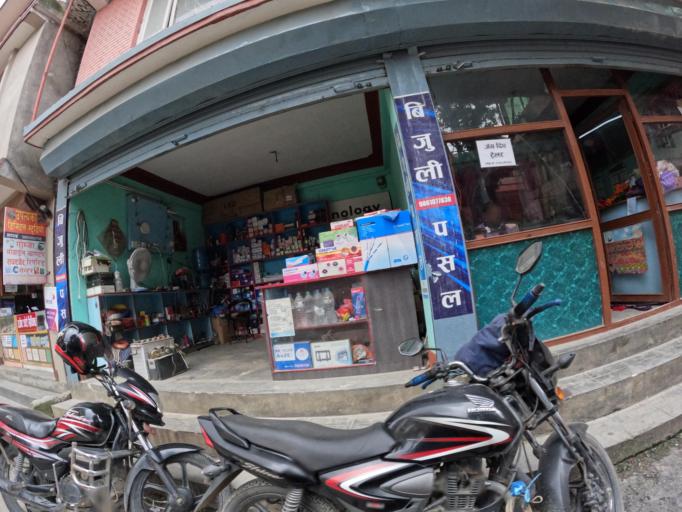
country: NP
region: Central Region
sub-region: Bagmati Zone
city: Kathmandu
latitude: 27.7381
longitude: 85.3180
